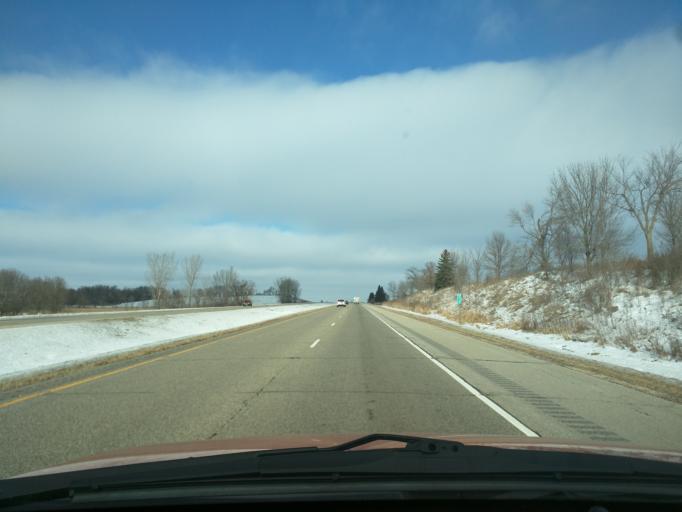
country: US
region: Minnesota
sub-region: Goodhue County
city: Pine Island
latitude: 44.2252
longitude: -92.6505
